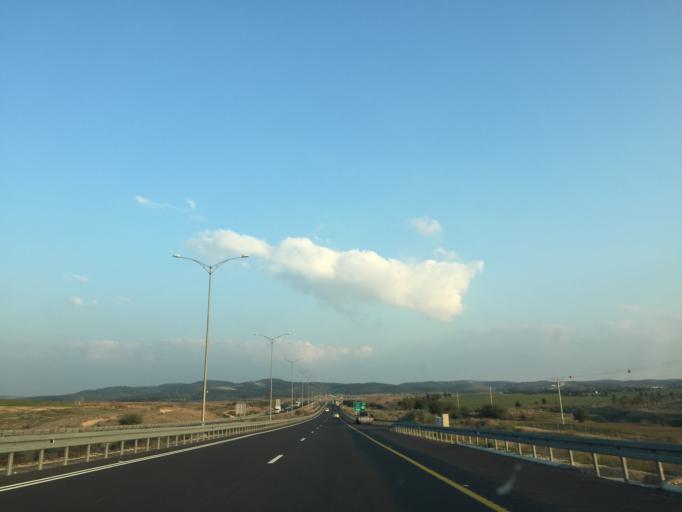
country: IL
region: Southern District
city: Lehavim
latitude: 31.3872
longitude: 34.8041
